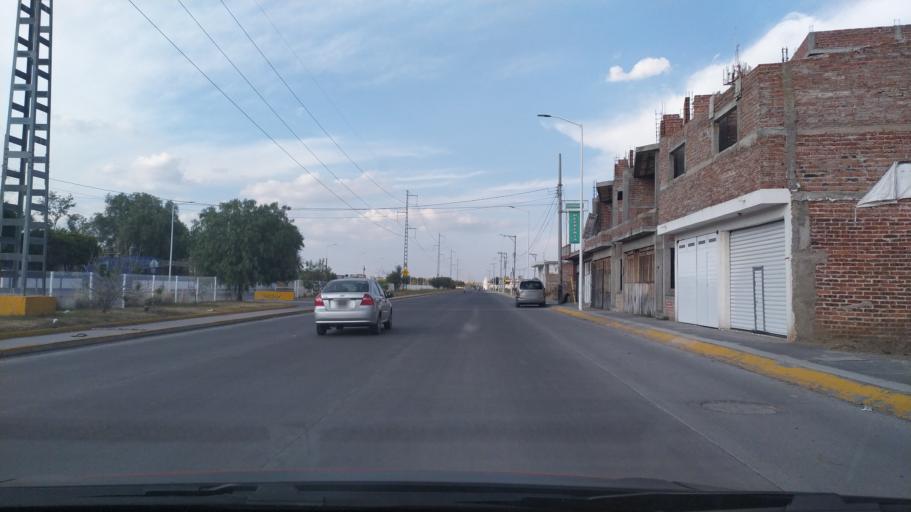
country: MX
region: Guanajuato
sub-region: Purisima del Rincon
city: Monte Grande
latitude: 21.0089
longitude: -101.8699
